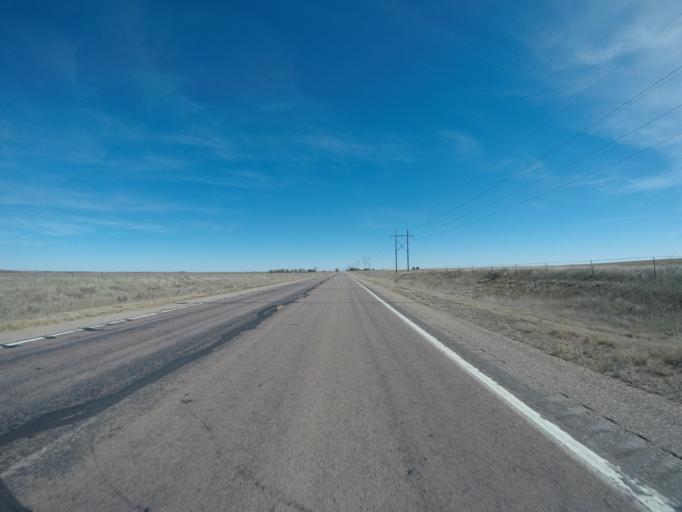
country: US
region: Colorado
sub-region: Yuma County
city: Yuma
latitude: 39.6552
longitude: -102.8347
